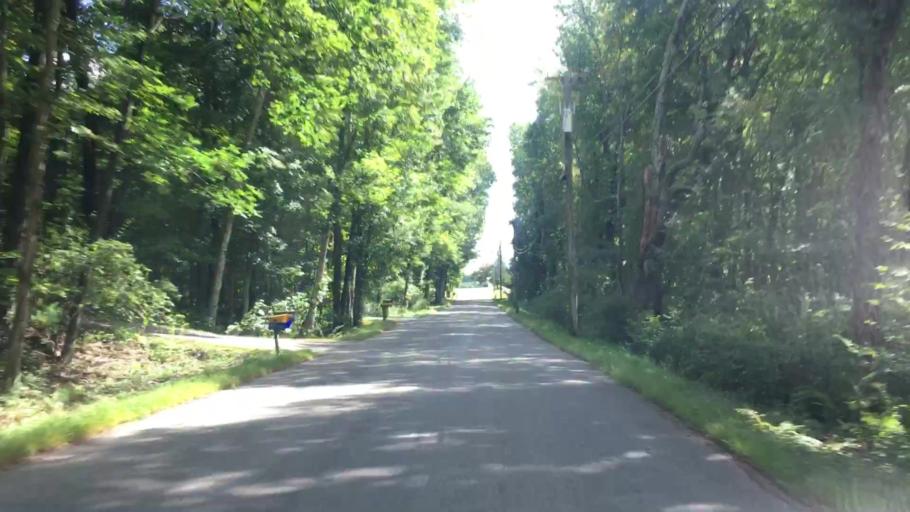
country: US
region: Connecticut
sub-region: Tolland County
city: Stafford Springs
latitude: 41.9175
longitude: -72.2109
